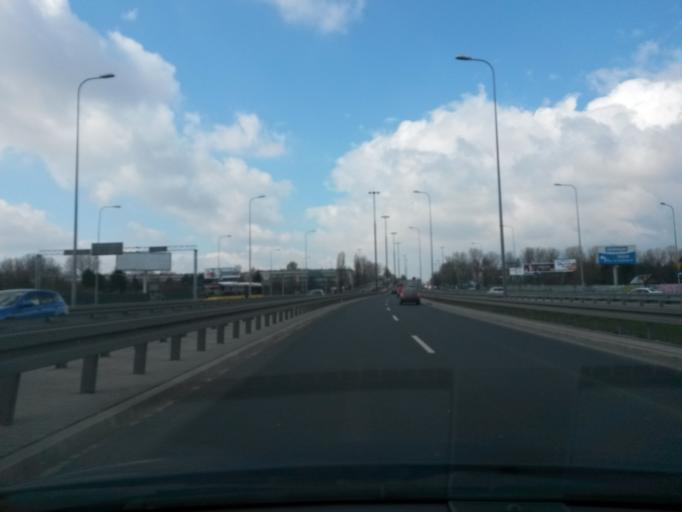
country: PL
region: Masovian Voivodeship
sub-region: Warszawa
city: Wlochy
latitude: 52.1823
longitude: 20.9832
